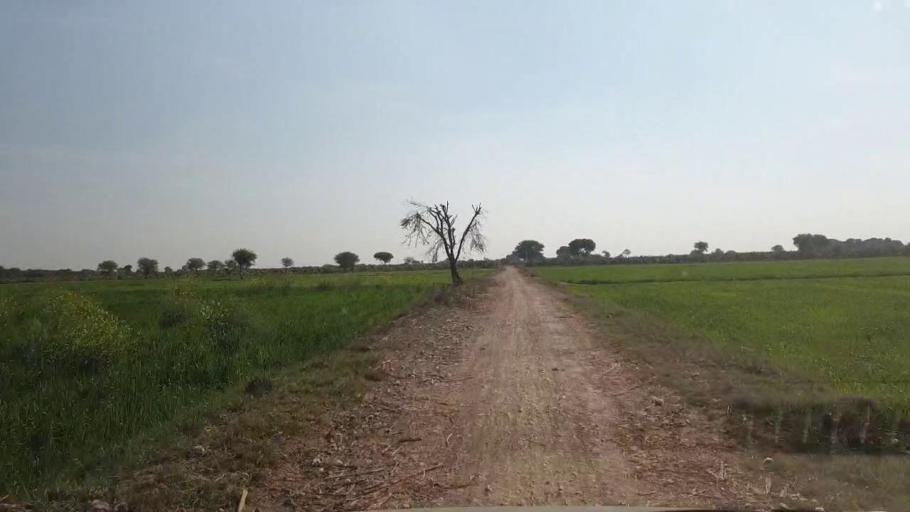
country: PK
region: Sindh
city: Chambar
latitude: 25.3253
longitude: 68.7938
